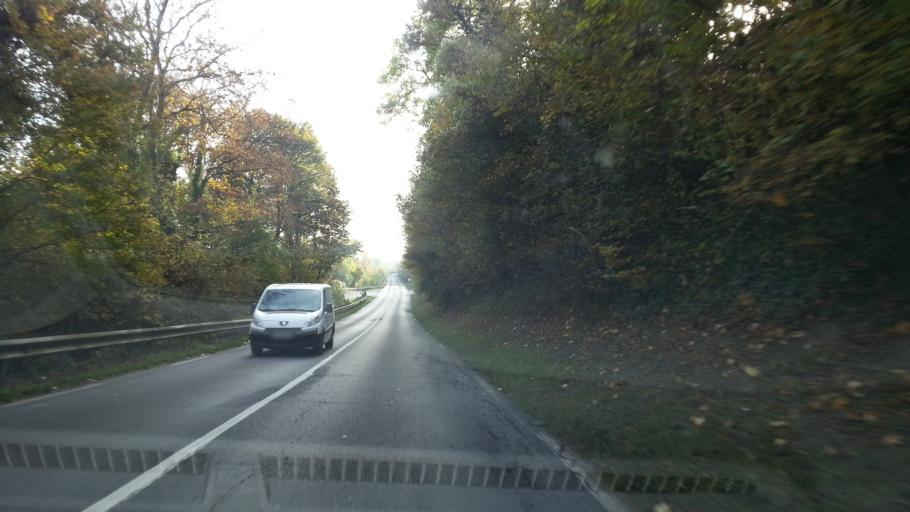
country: FR
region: Picardie
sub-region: Departement de l'Oise
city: Precy-sur-Oise
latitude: 49.1925
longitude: 2.3647
